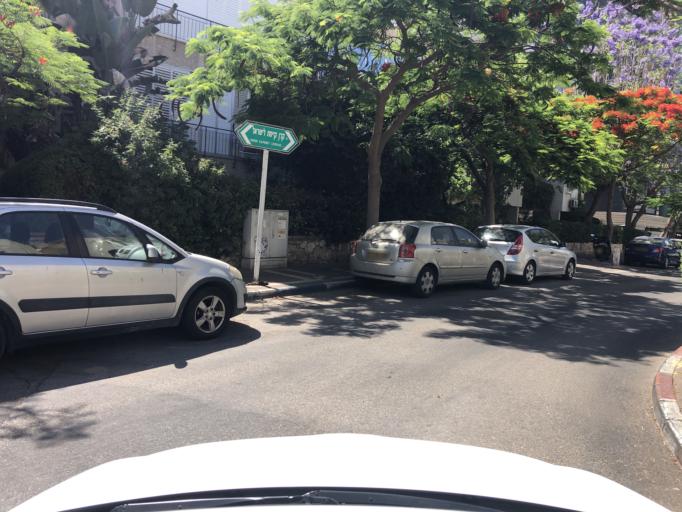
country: IL
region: Tel Aviv
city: Ramat Gan
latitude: 32.0763
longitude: 34.8064
